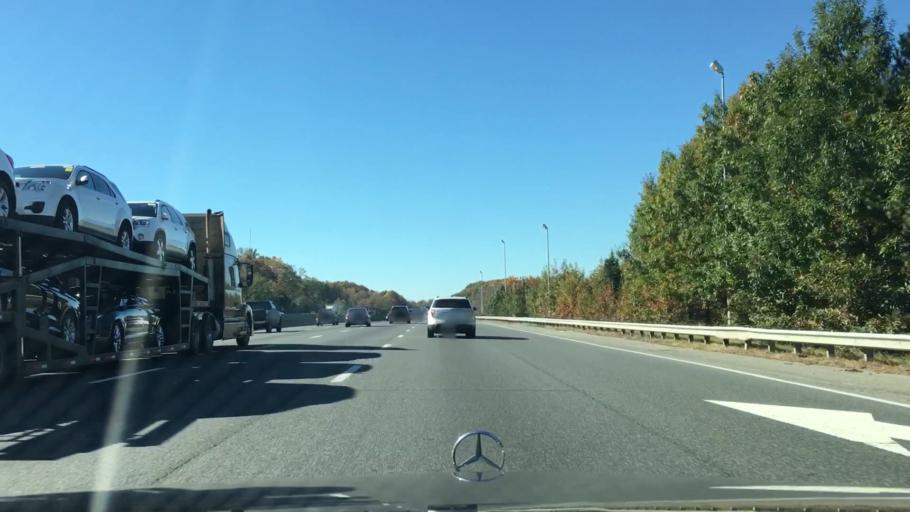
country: US
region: Virginia
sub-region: Fairfax County
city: Rose Hill
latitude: 38.8020
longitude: -77.1138
